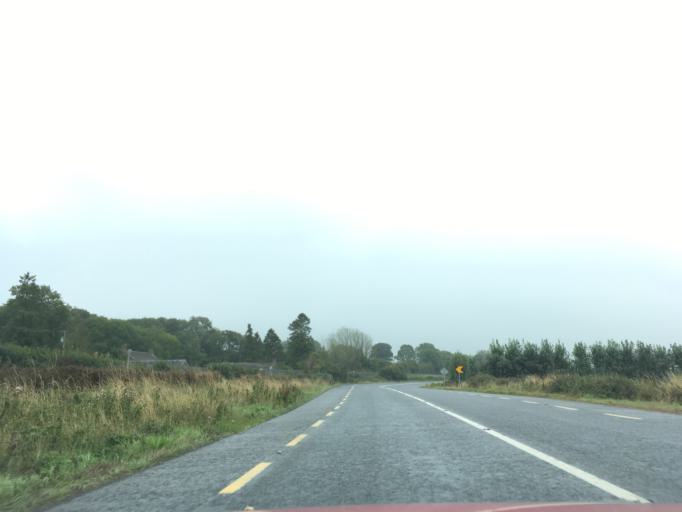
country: IE
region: Munster
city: Carrick-on-Suir
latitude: 52.3525
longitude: -7.4723
